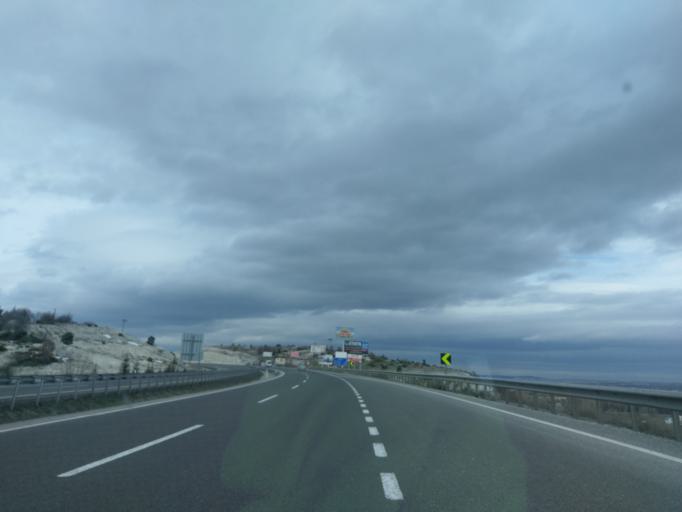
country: TR
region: Kuetahya
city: Kutahya
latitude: 39.3723
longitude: 30.0663
